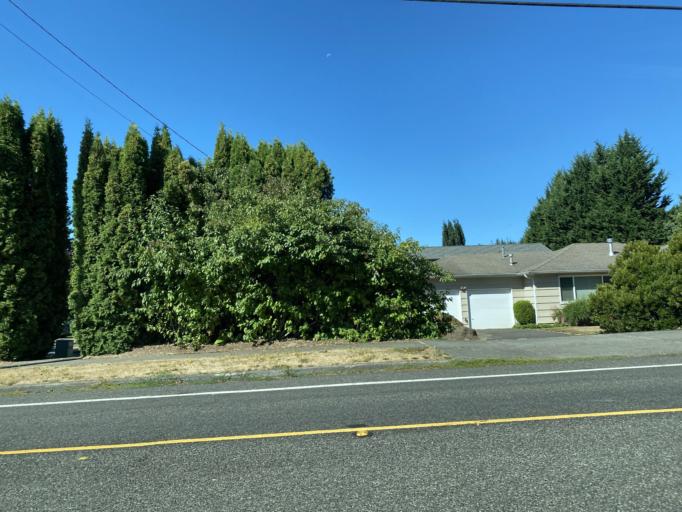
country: US
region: Washington
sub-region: Thurston County
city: Tumwater
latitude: 47.0089
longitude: -122.8652
